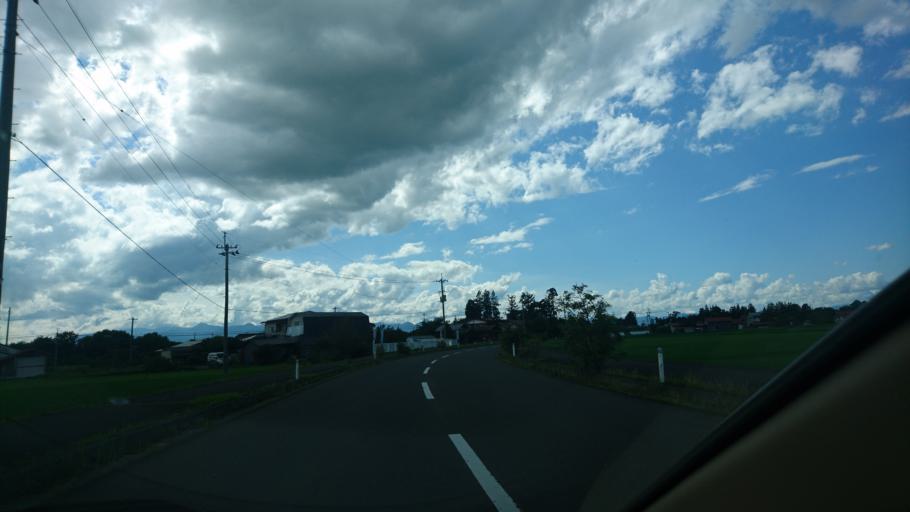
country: JP
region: Iwate
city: Mizusawa
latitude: 39.1925
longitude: 141.1645
